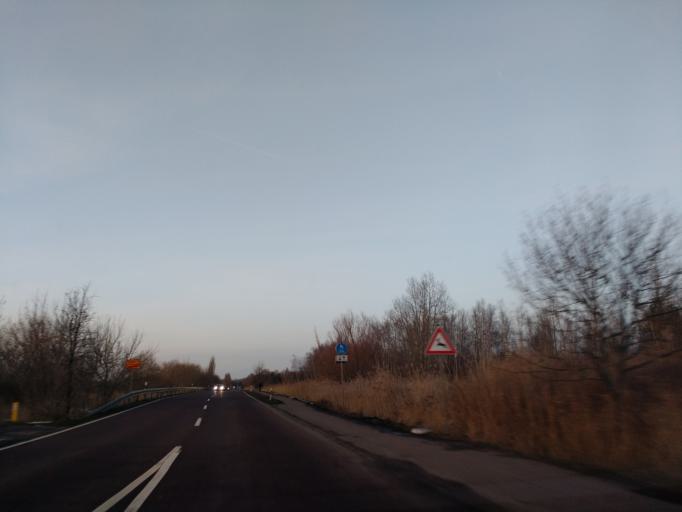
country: DE
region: Saxony-Anhalt
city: Sennewitz
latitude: 51.5283
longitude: 11.9563
